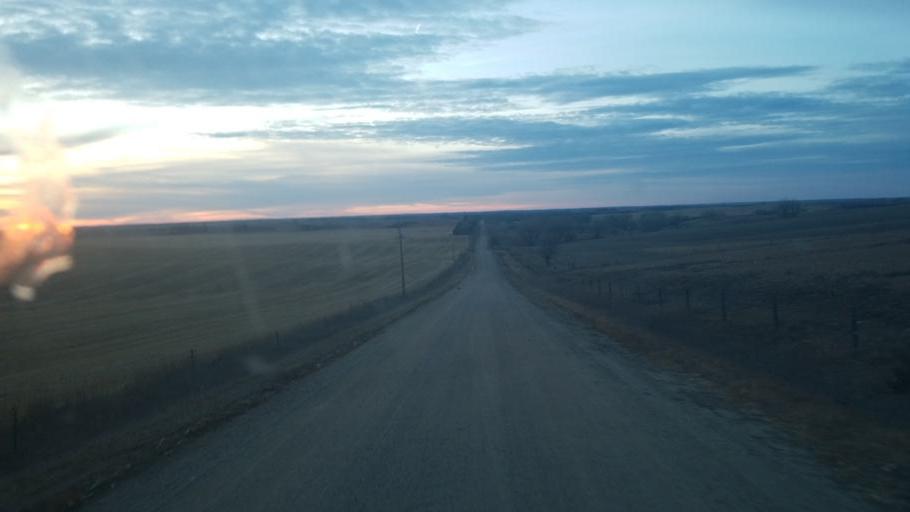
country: US
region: Nebraska
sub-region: Knox County
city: Center
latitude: 42.6554
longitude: -97.7604
